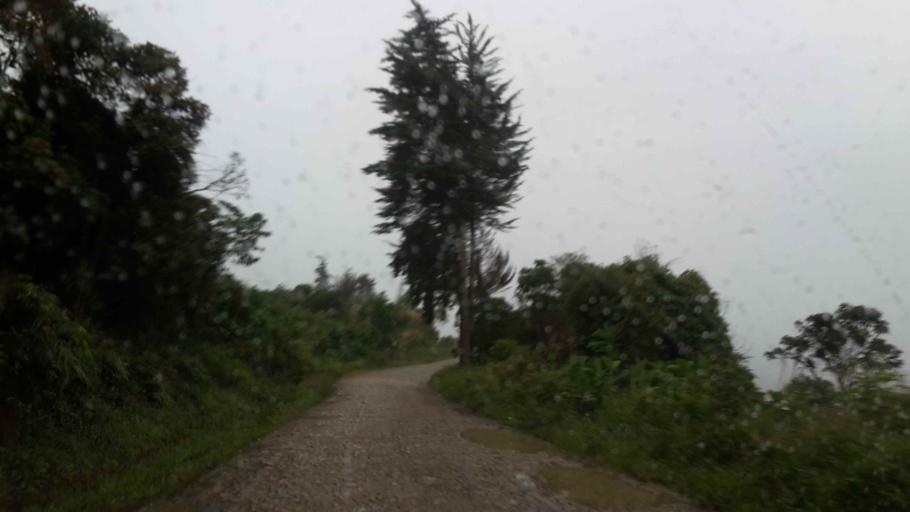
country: BO
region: Cochabamba
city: Colomi
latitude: -17.1415
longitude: -65.9195
